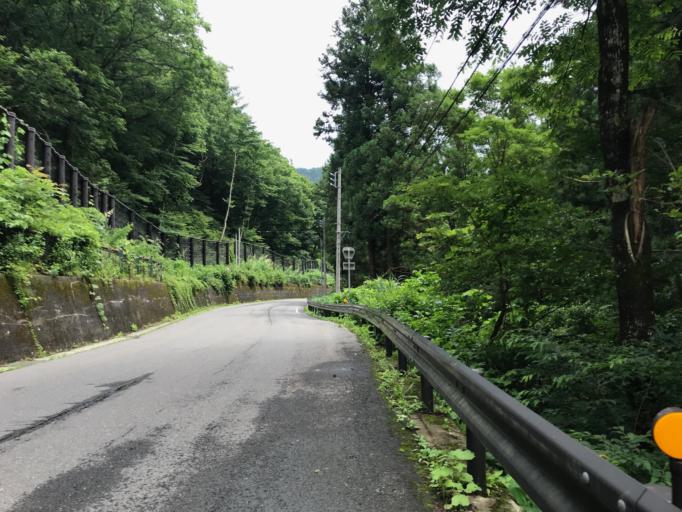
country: JP
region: Gunma
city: Numata
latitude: 36.8209
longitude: 138.9794
